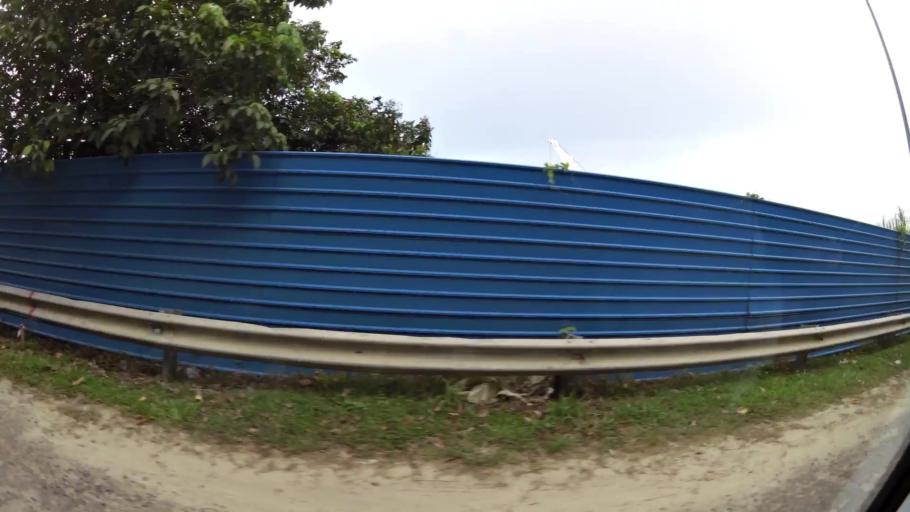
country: BN
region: Brunei and Muara
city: Bandar Seri Begawan
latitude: 4.9272
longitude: 115.0137
